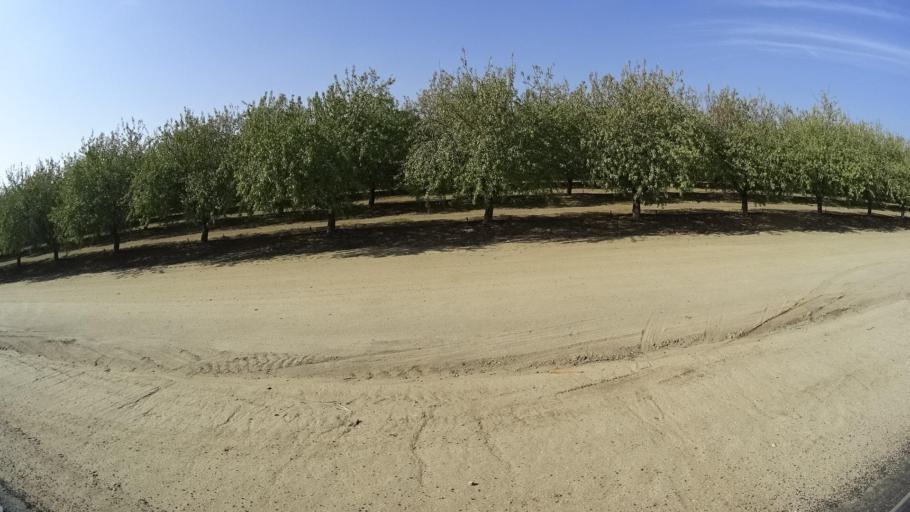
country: US
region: California
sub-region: Kern County
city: Shafter
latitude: 35.5542
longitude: -119.1513
